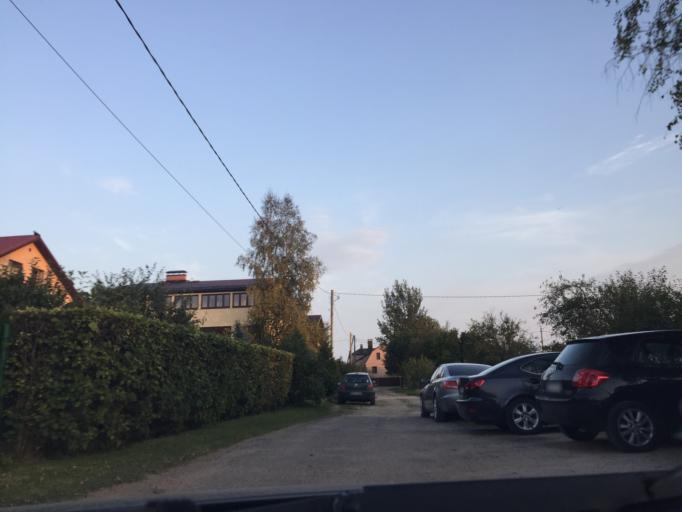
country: LV
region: Salaspils
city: Salaspils
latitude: 56.9211
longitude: 24.4251
